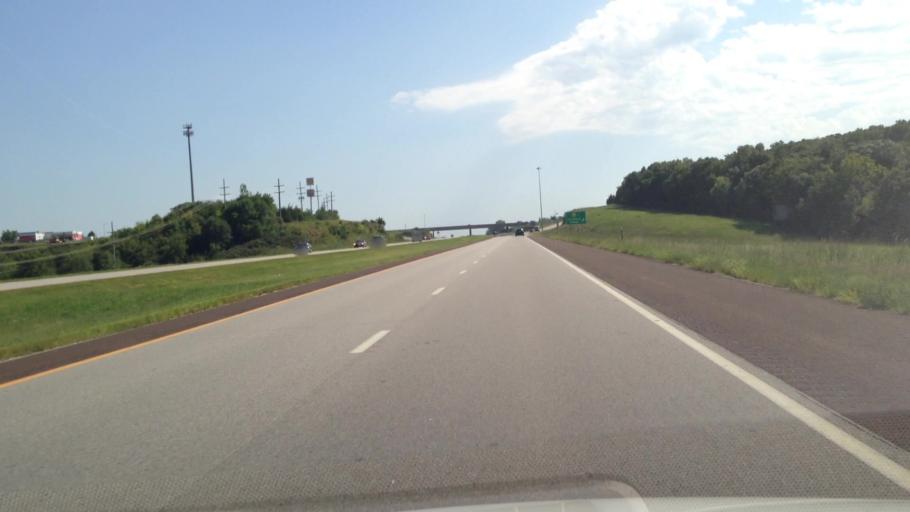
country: US
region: Kansas
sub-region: Miami County
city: Louisburg
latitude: 38.6276
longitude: -94.6949
